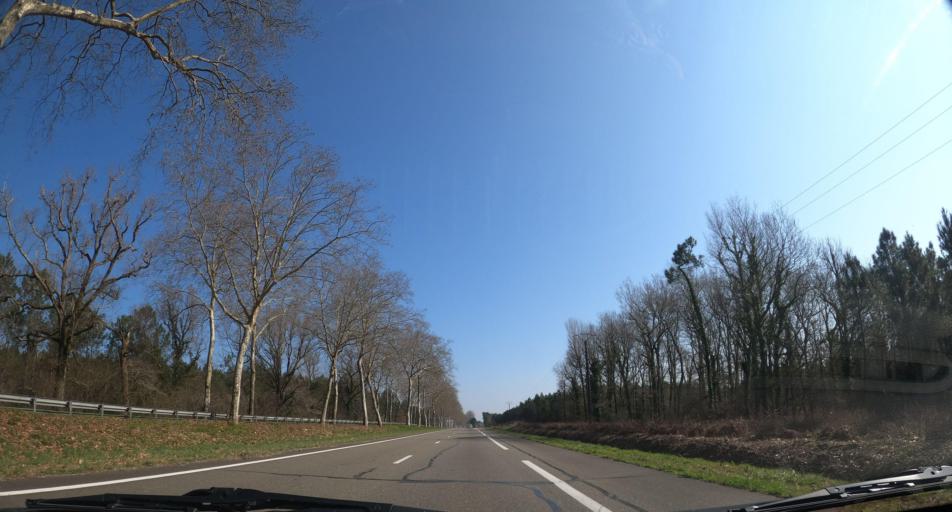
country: FR
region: Aquitaine
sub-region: Departement des Landes
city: Riviere-Saas-et-Gourby
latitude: 43.7134
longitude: -1.1459
